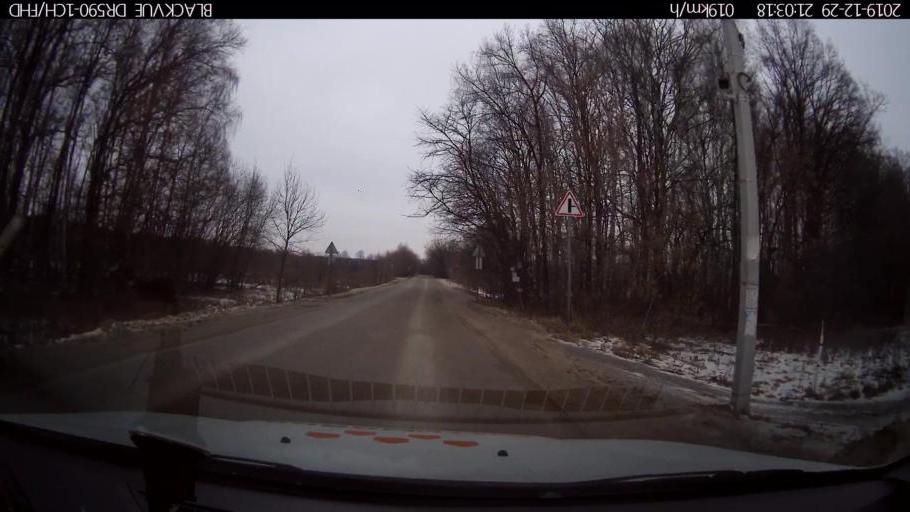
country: RU
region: Nizjnij Novgorod
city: Afonino
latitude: 56.1944
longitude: 44.0052
